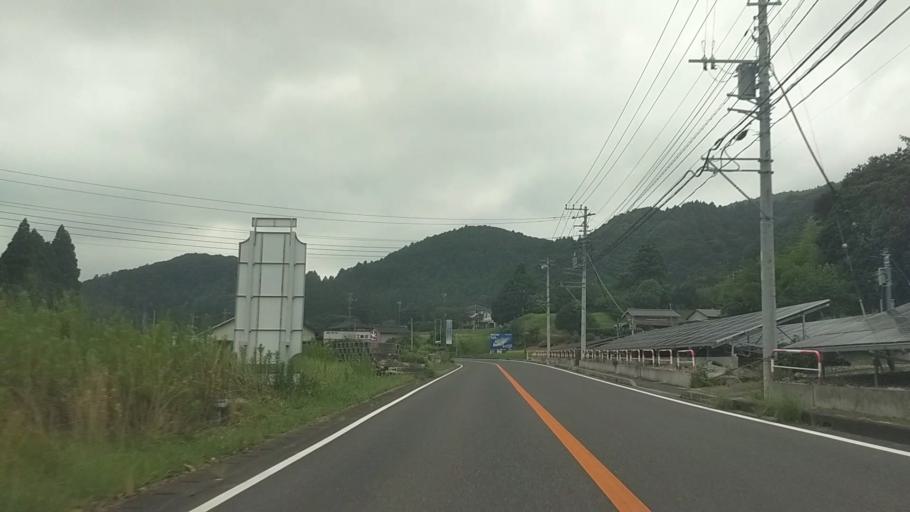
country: JP
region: Chiba
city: Kawaguchi
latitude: 35.1423
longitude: 139.9726
